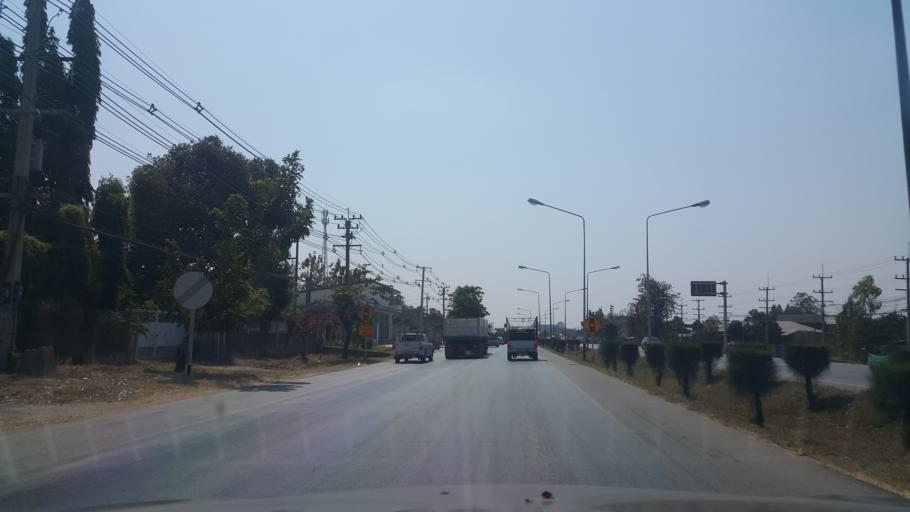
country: TH
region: Khon Kaen
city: Ban Phai
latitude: 16.0731
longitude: 102.7223
